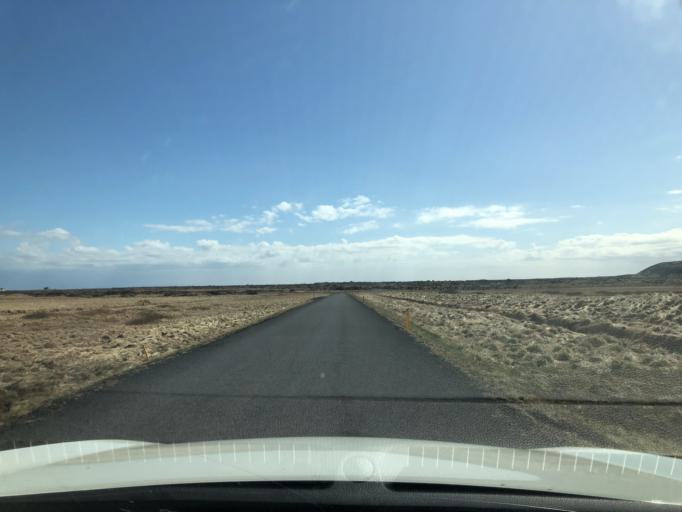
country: IS
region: West
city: Olafsvik
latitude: 64.8328
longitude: -23.4069
